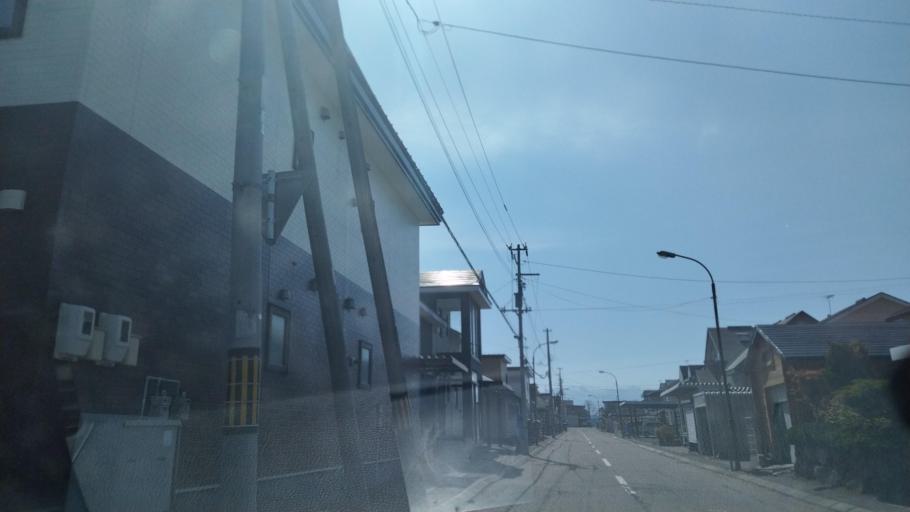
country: JP
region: Hokkaido
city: Obihiro
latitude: 42.9174
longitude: 143.0582
